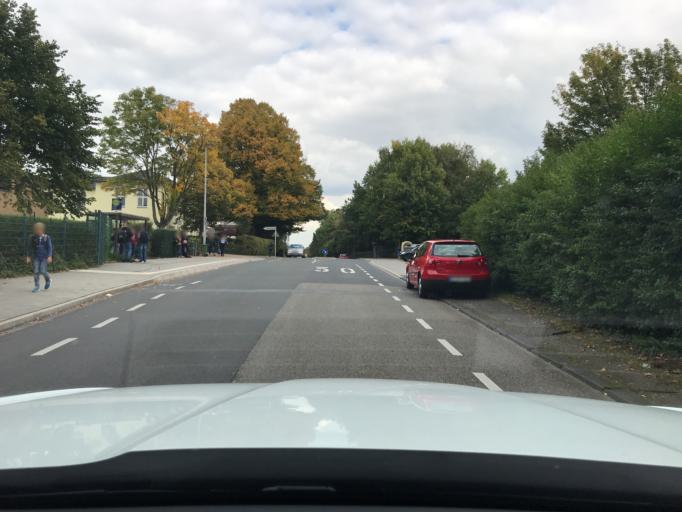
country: DE
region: North Rhine-Westphalia
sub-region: Regierungsbezirk Dusseldorf
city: Muelheim (Ruhr)
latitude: 51.4195
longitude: 6.8652
